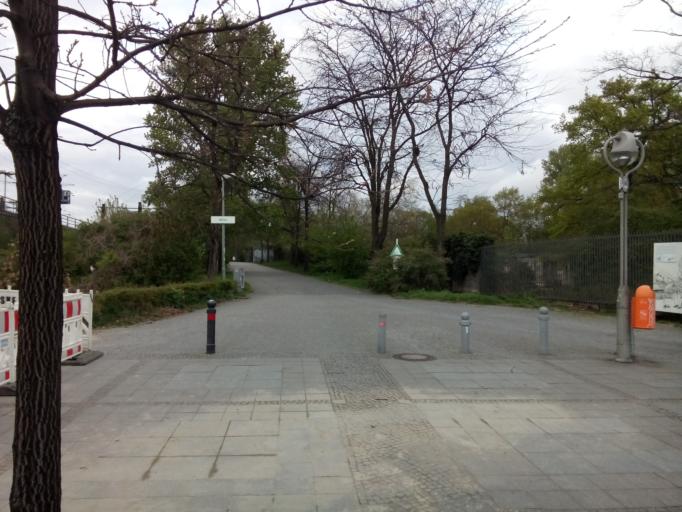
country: DE
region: Berlin
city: Hansaviertel
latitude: 52.5087
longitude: 13.3342
